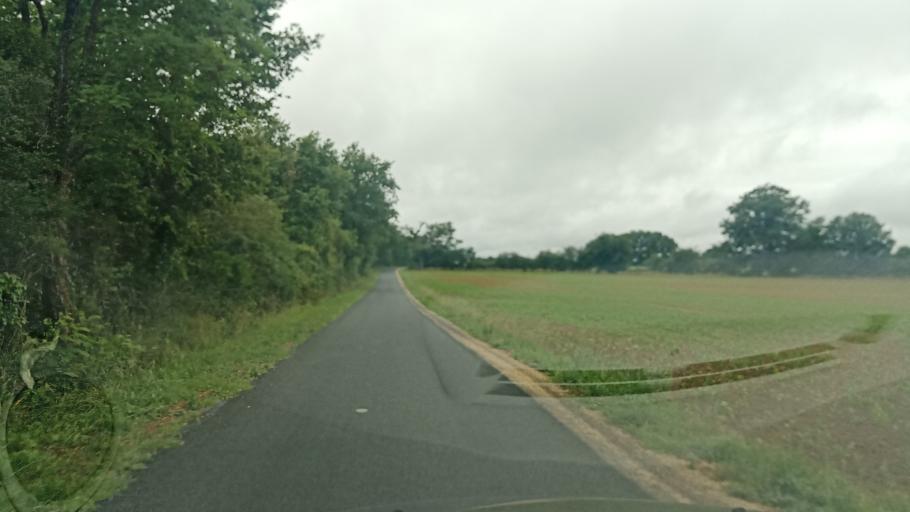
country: FR
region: Poitou-Charentes
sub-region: Departement de la Vienne
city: Biard
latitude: 46.5921
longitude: 0.2943
